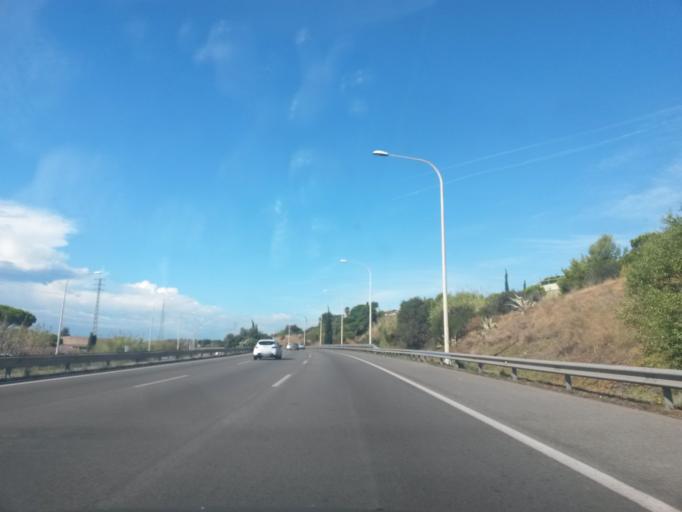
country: ES
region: Catalonia
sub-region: Provincia de Barcelona
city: Premia de Mar
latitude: 41.5034
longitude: 2.3569
